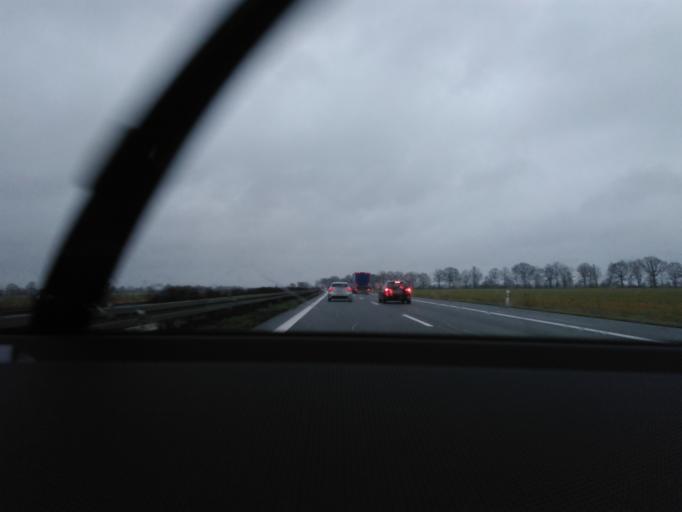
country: DE
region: Brandenburg
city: Heiligengrabe
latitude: 53.1798
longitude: 12.3016
